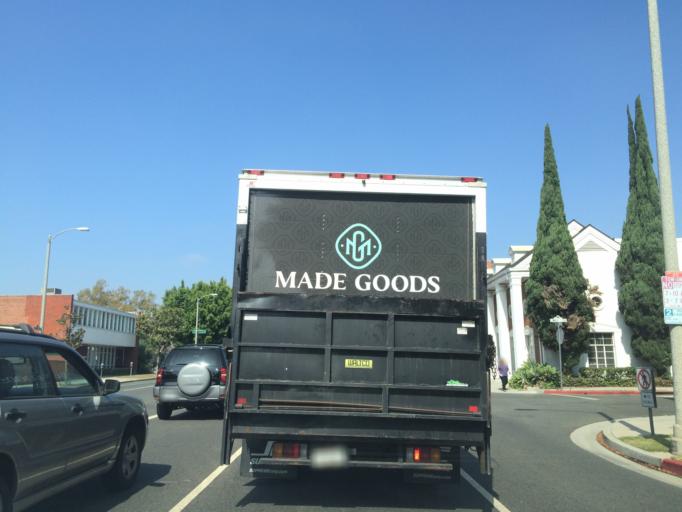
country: US
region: California
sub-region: Los Angeles County
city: Beverly Hills
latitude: 34.0594
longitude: -118.3854
